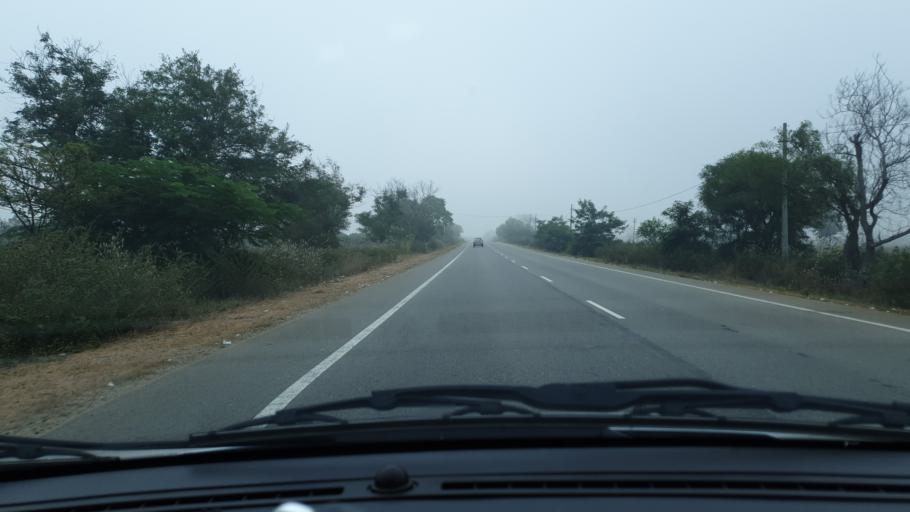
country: IN
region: Telangana
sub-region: Nalgonda
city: Devarkonda
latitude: 16.6338
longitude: 78.6396
